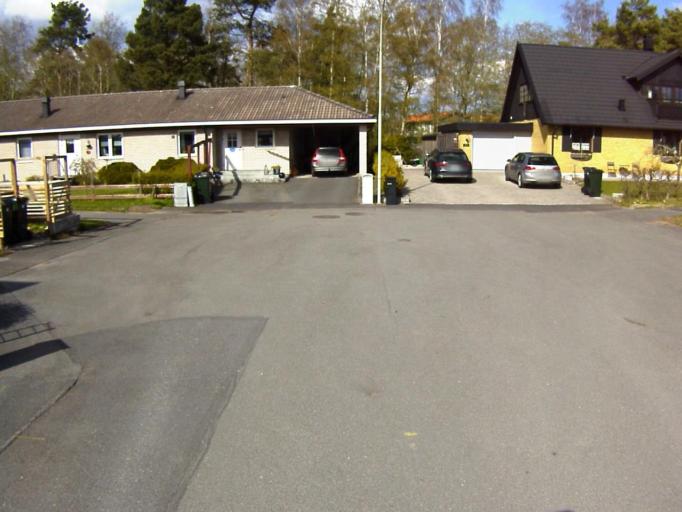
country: SE
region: Skane
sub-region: Kristianstads Kommun
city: Norra Asum
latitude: 56.0065
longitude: 14.0859
